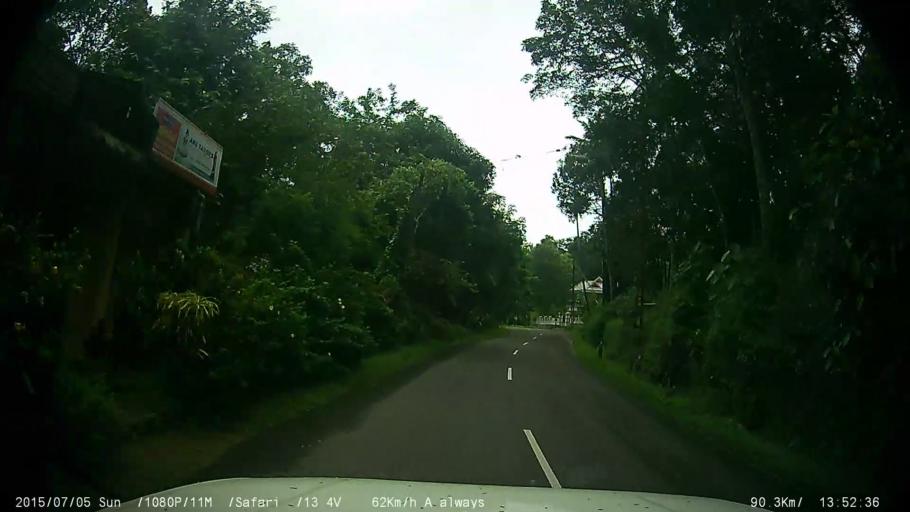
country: IN
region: Kerala
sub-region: Kottayam
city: Palackattumala
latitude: 9.7498
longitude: 76.6056
